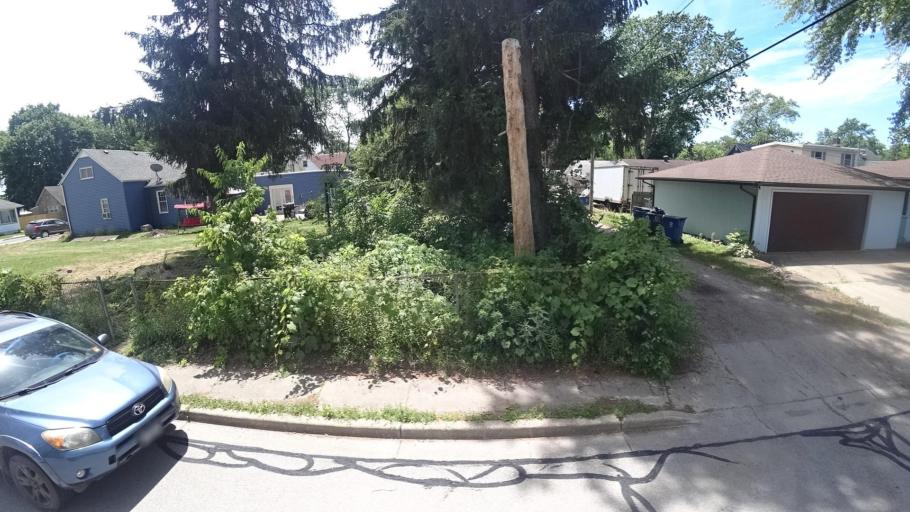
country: US
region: Indiana
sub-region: Porter County
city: Porter
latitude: 41.6181
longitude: -87.0745
